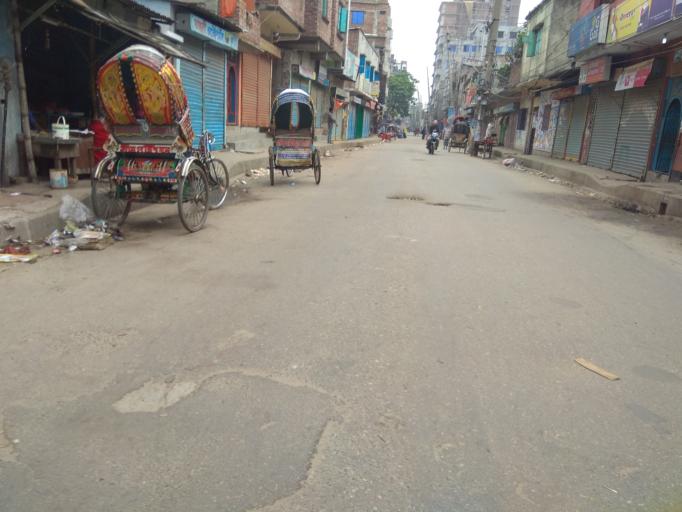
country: BD
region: Dhaka
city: Azimpur
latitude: 23.7130
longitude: 90.3712
